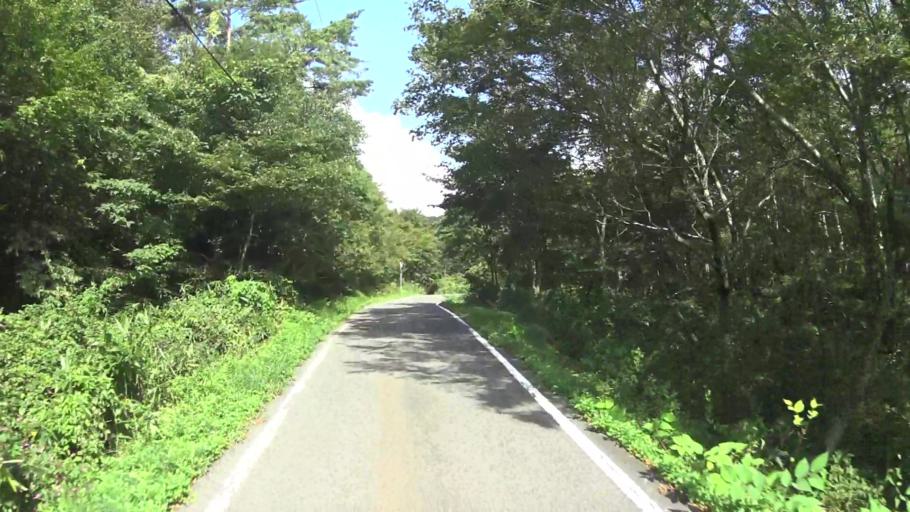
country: JP
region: Kyoto
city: Miyazu
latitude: 35.6471
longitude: 135.1802
